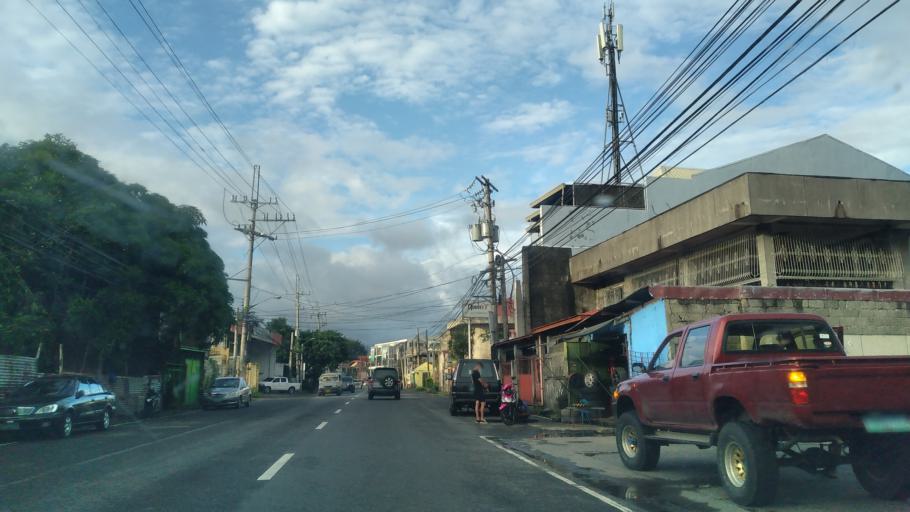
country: PH
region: Calabarzon
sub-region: Province of Quezon
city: Lucena
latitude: 13.9482
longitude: 121.6141
